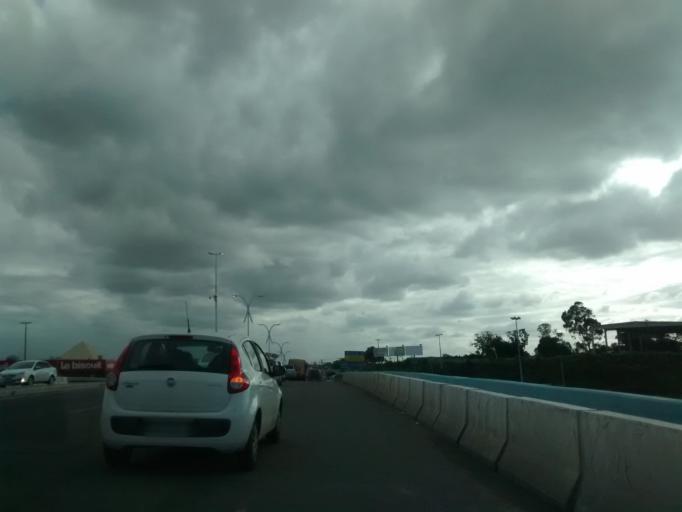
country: BR
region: Bahia
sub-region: Lauro De Freitas
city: Lauro de Freitas
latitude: -12.9212
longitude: -38.3536
